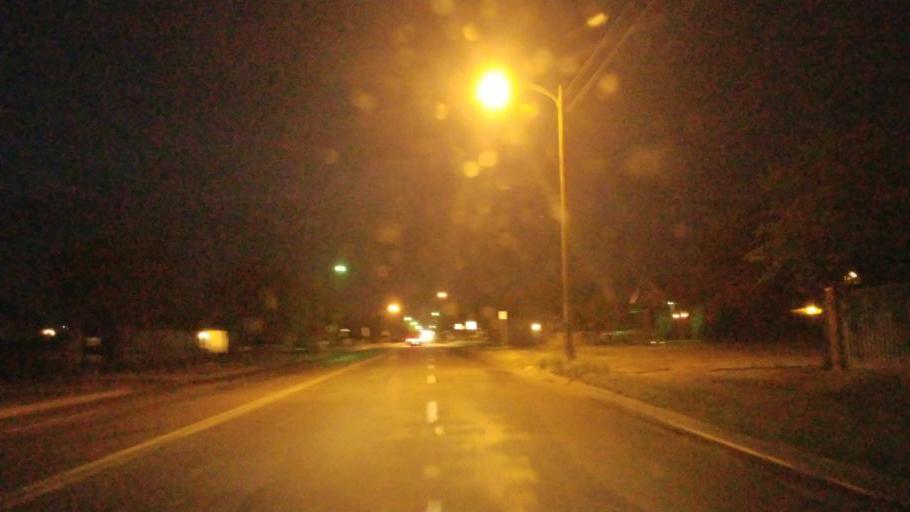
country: US
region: Texas
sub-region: Potter County
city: Amarillo
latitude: 35.1944
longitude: -101.8267
